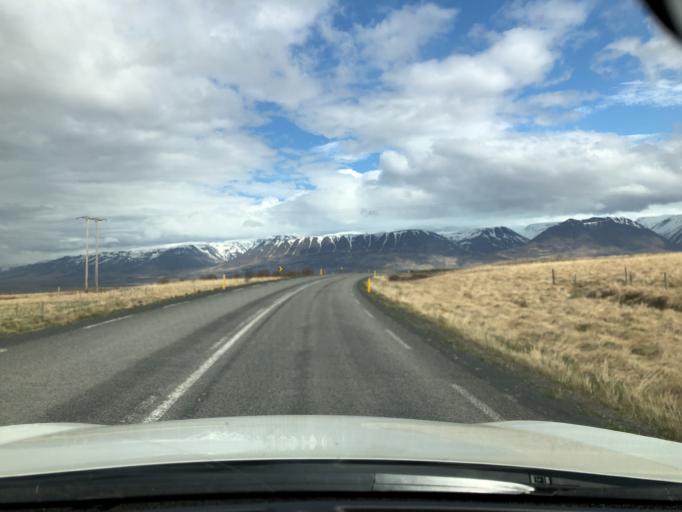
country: IS
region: Northwest
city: Saudarkrokur
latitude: 65.5480
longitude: -19.4902
